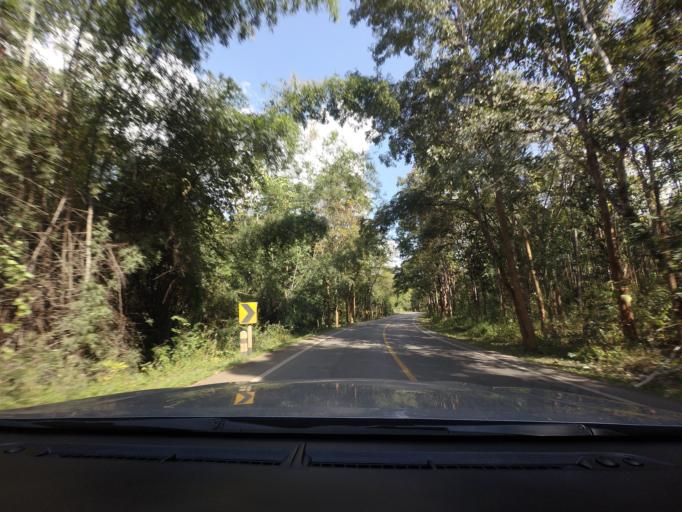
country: TH
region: Chiang Mai
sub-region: Amphoe Chiang Dao
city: Chiang Dao
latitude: 19.4966
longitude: 99.0368
